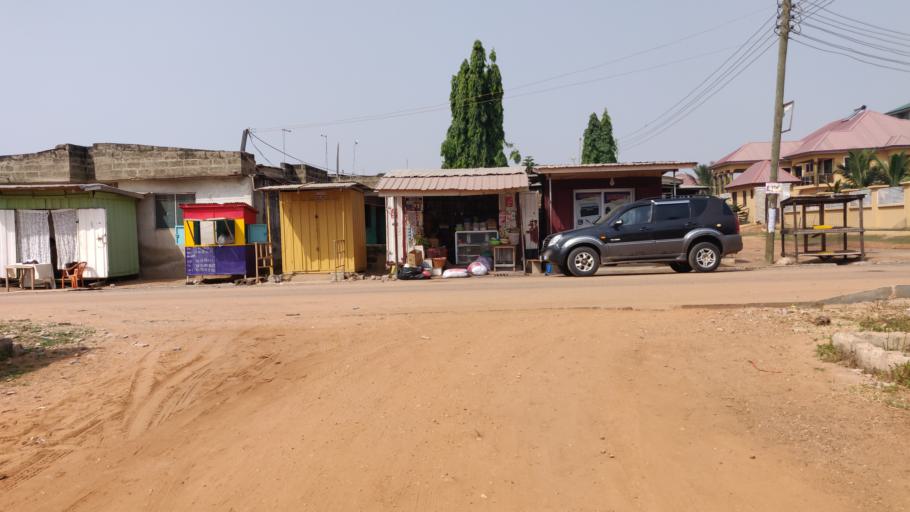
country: GH
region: Greater Accra
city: Nungua
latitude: 5.6205
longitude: -0.0828
